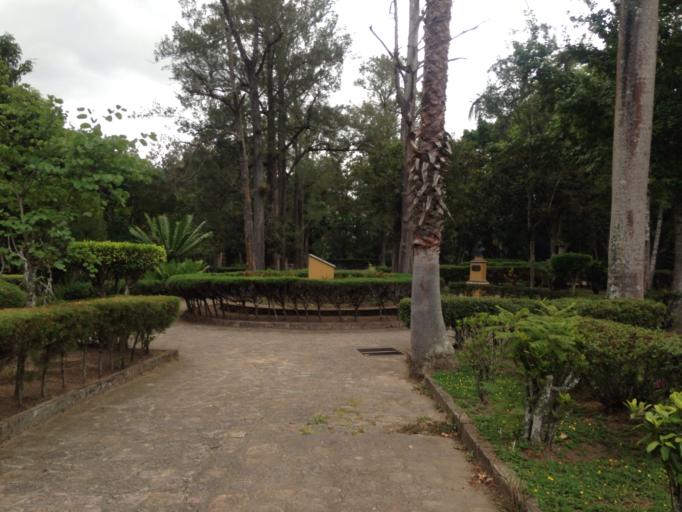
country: HN
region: Francisco Morazan
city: Tegucigalpa
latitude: 14.1193
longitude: -87.1956
